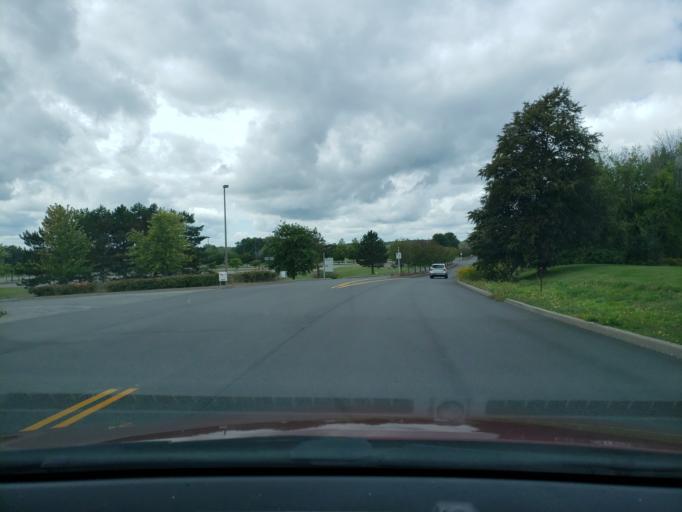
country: US
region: New York
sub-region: Monroe County
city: North Gates
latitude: 43.1570
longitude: -77.7459
